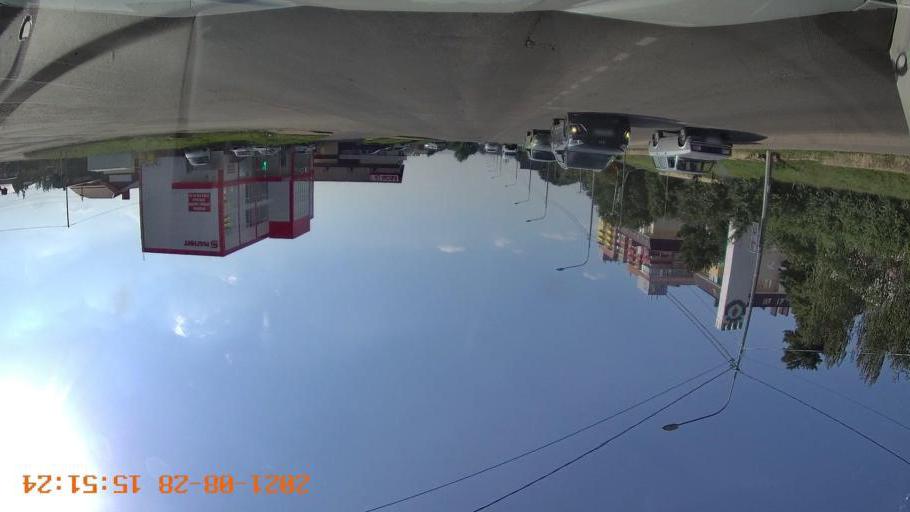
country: RU
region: Stavropol'skiy
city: Tatarka
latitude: 44.9848
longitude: 41.9208
